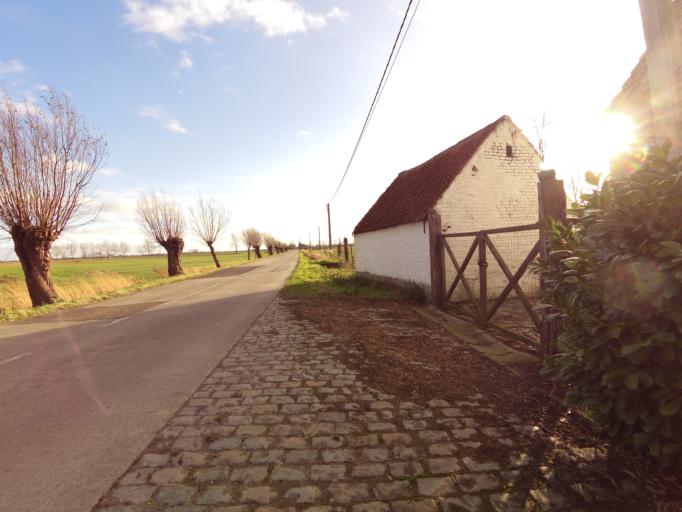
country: BE
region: Flanders
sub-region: Provincie West-Vlaanderen
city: Middelkerke
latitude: 51.1537
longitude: 2.8862
